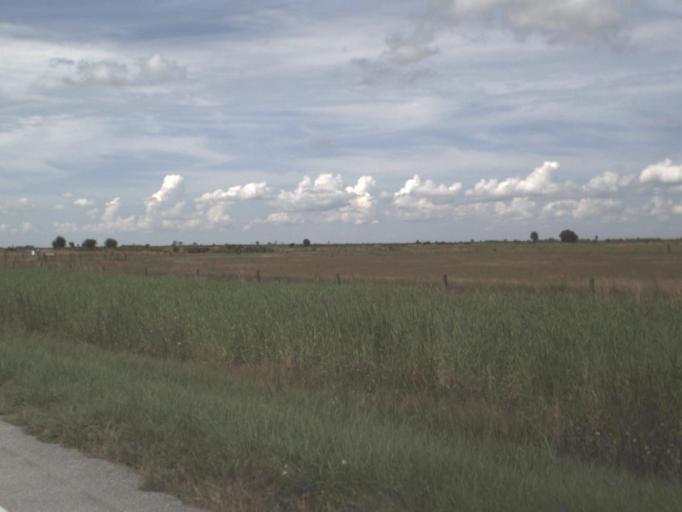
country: US
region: Florida
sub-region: Highlands County
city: Placid Lakes
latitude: 27.2092
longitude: -81.5375
